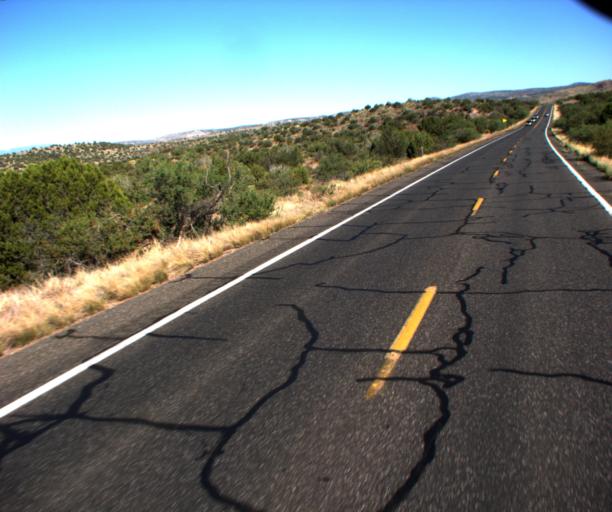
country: US
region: Arizona
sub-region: Yavapai County
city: Lake Montezuma
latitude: 34.7058
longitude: -111.7716
